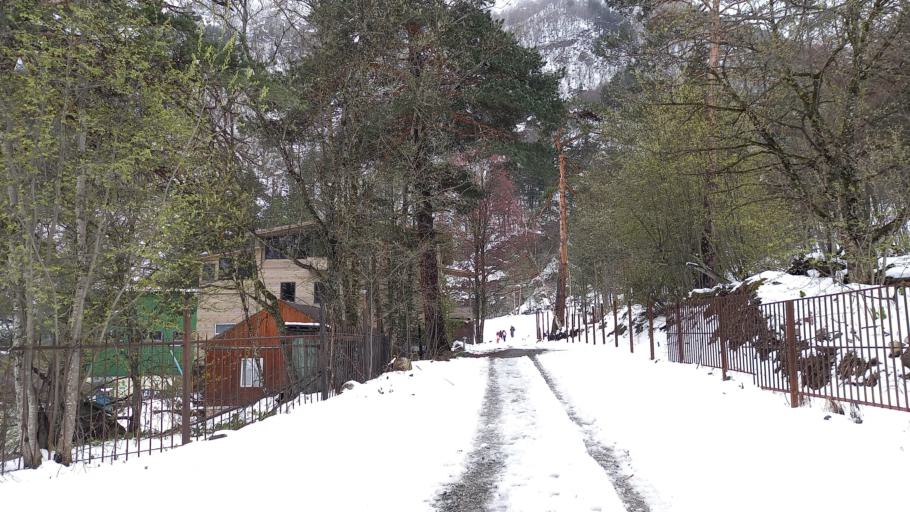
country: RU
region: North Ossetia
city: Mizur
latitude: 42.7854
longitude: 43.9044
